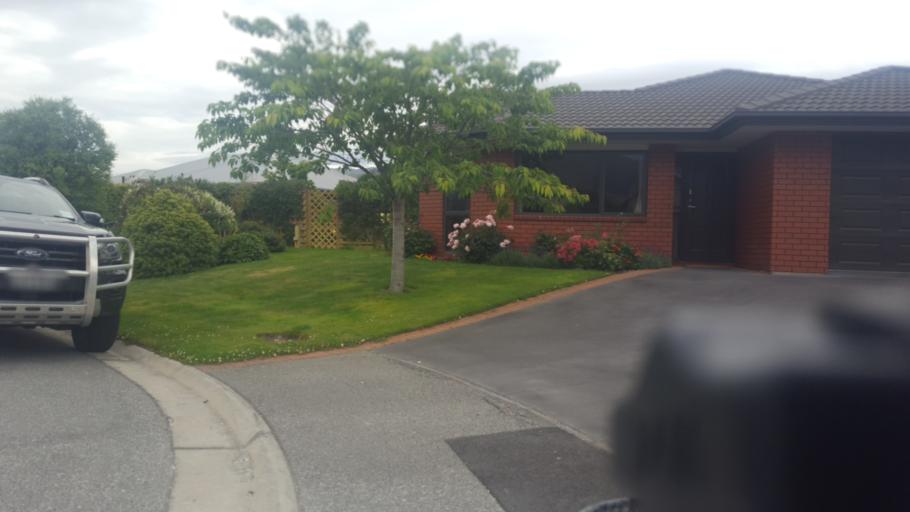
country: NZ
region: Otago
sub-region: Queenstown-Lakes District
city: Wanaka
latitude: -45.0480
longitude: 169.1864
